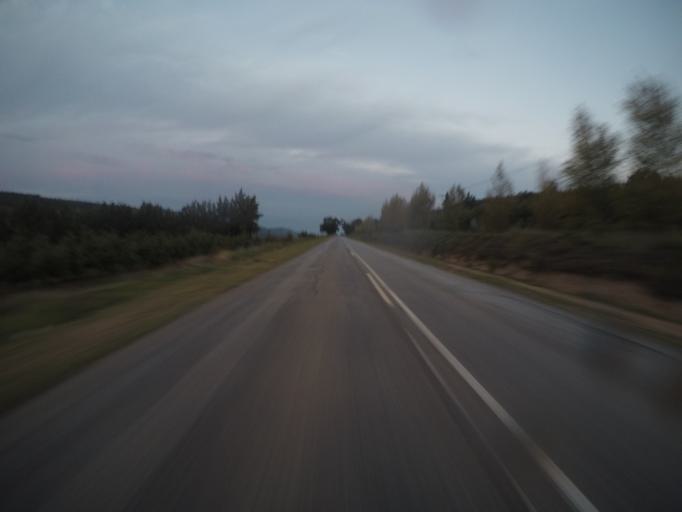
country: ZA
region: Western Cape
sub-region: Eden District Municipality
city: Plettenberg Bay
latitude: -33.8043
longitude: 23.6700
